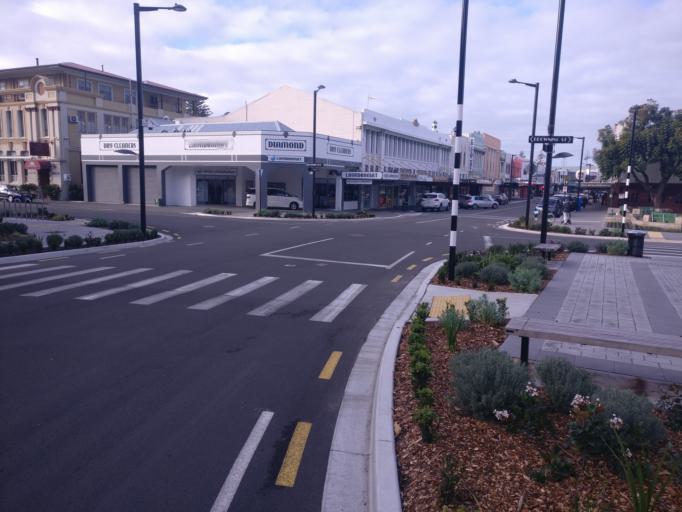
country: NZ
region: Hawke's Bay
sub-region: Napier City
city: Napier
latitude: -39.4882
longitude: 176.9175
